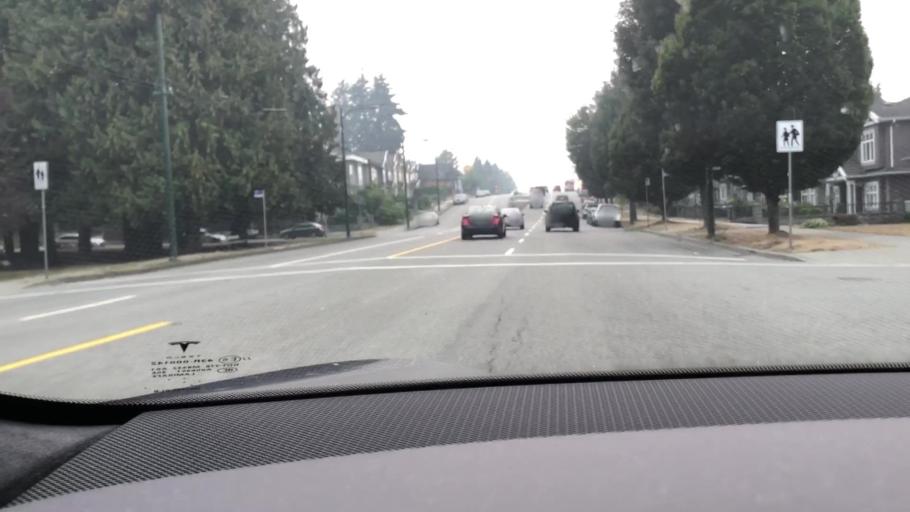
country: CA
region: British Columbia
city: Vancouver
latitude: 49.2329
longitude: -123.0868
